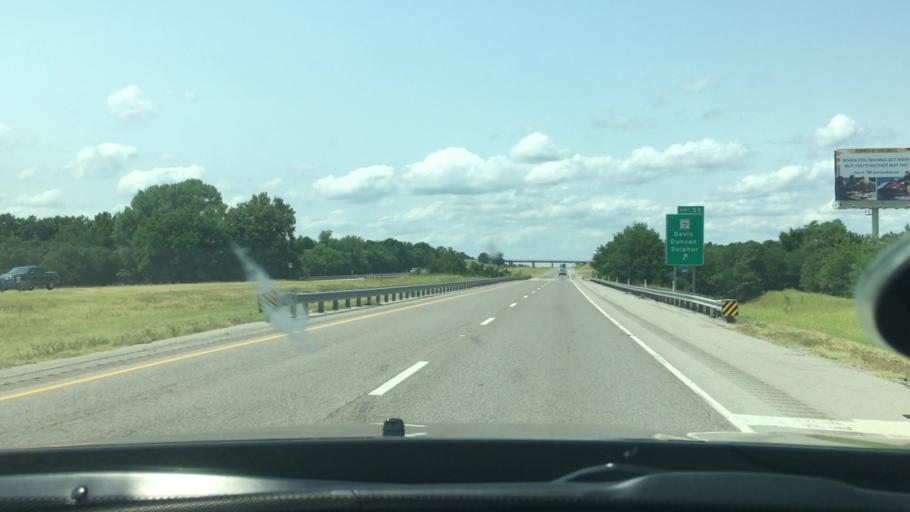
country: US
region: Oklahoma
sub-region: Murray County
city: Davis
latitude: 34.4995
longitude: -97.1693
